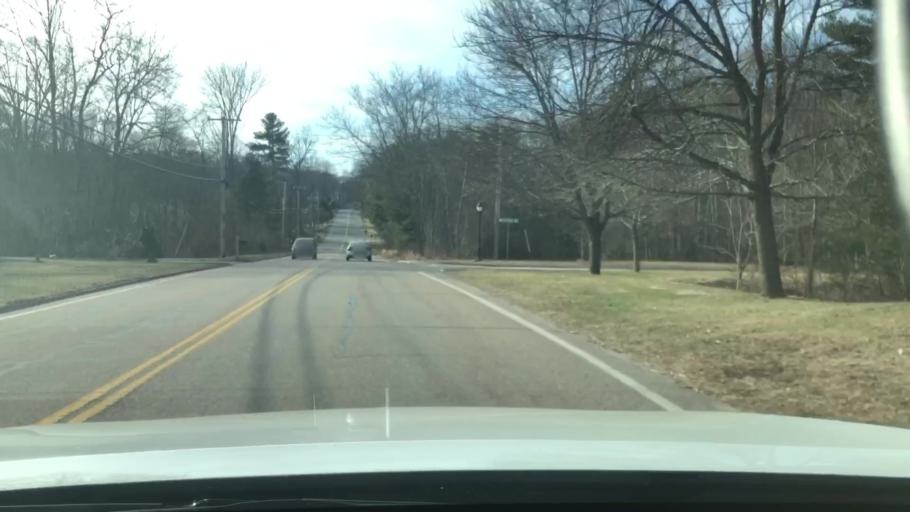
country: US
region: Massachusetts
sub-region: Worcester County
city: Millbury
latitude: 42.1979
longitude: -71.7232
